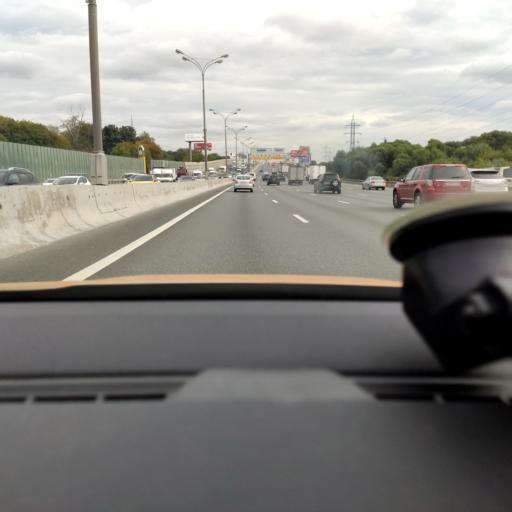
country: RU
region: Moscow
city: Yaroslavskiy
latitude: 55.8891
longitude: 37.7119
